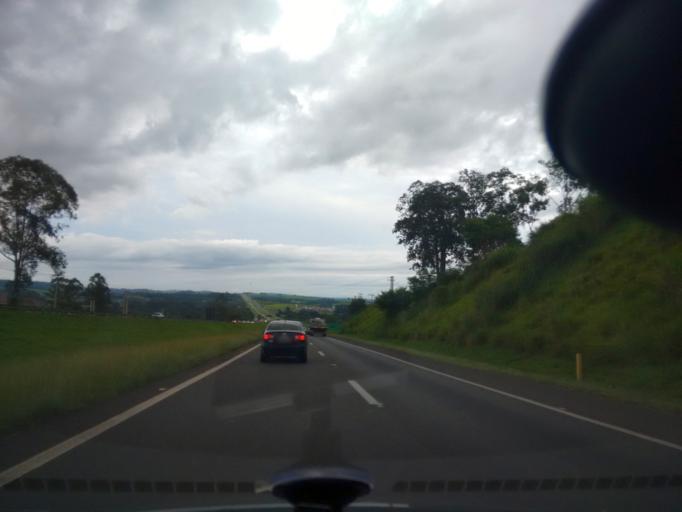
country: BR
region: Sao Paulo
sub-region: Rio Claro
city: Rio Claro
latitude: -22.4008
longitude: -47.5926
